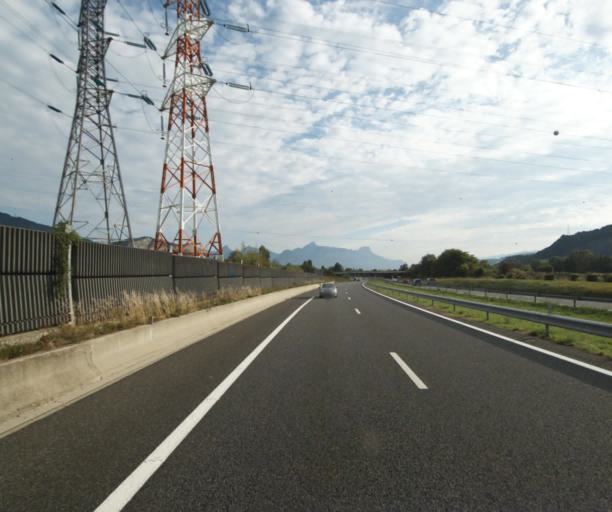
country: FR
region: Rhone-Alpes
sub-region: Departement de l'Isere
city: Allieres-et-Risset
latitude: 45.1078
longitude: 5.6787
